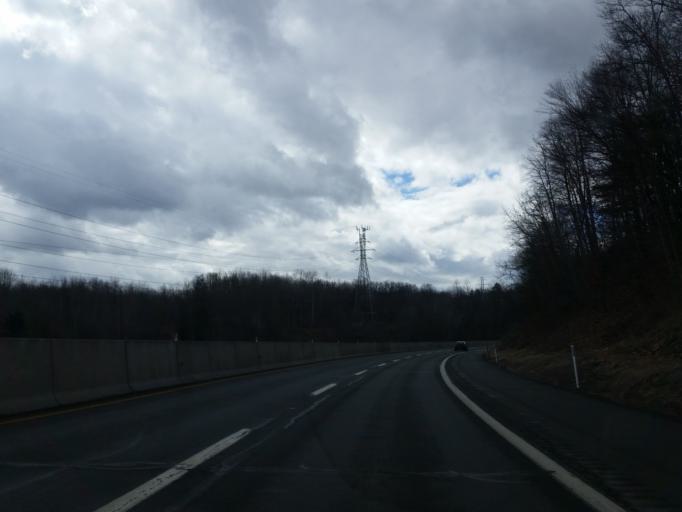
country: US
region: Pennsylvania
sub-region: Luzerne County
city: Avoca
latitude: 41.3384
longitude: -75.7084
